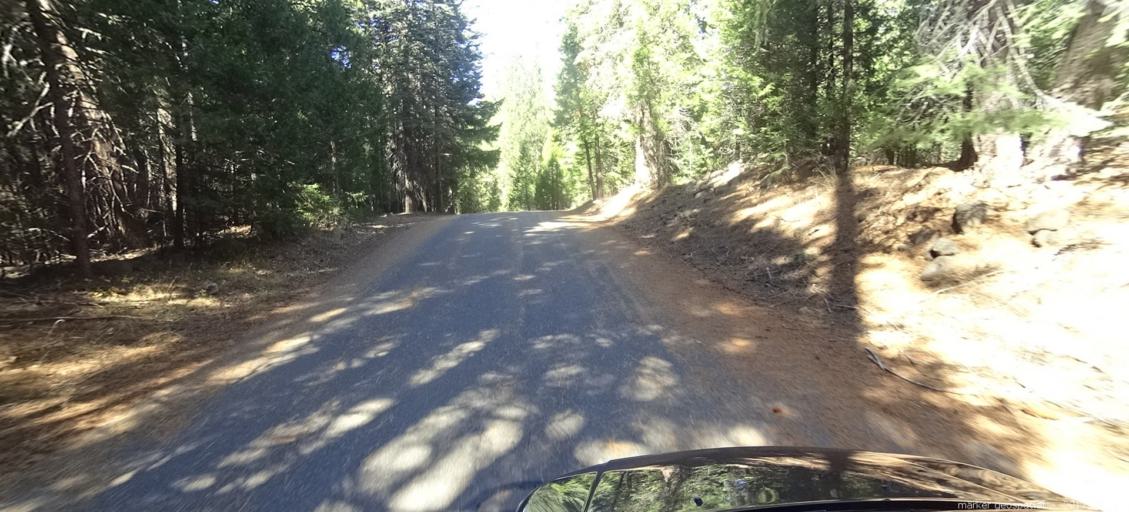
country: US
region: California
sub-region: Shasta County
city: Shingletown
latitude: 40.5007
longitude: -121.6595
